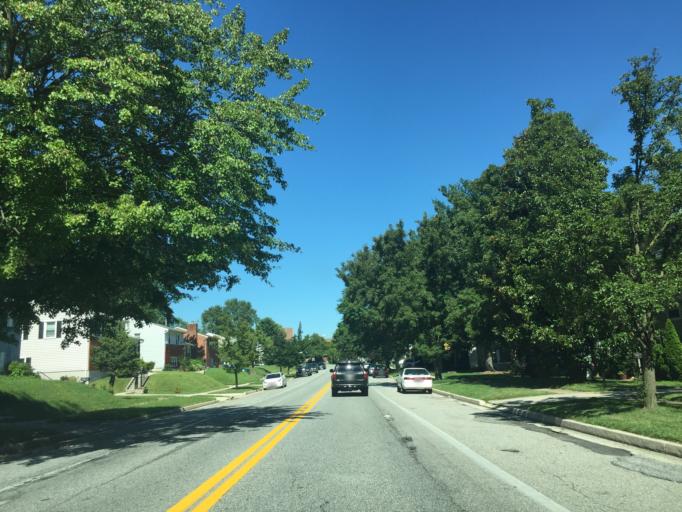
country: US
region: Maryland
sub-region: Baltimore County
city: Lutherville
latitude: 39.4128
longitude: -76.6244
